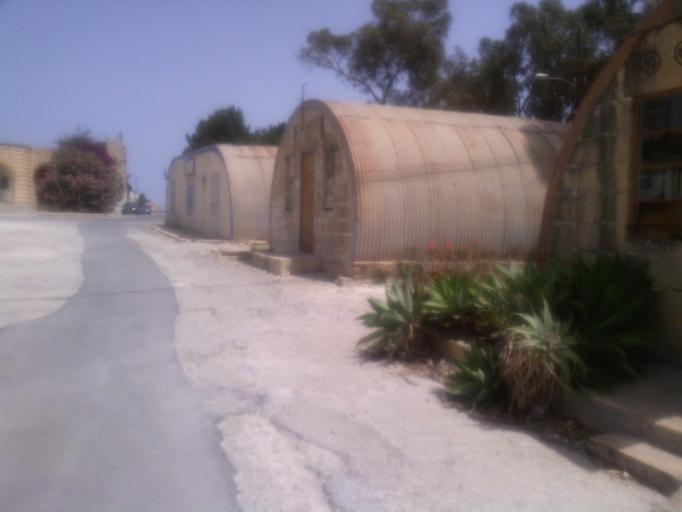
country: MT
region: L-Imdina
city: Imdina
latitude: 35.8909
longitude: 14.4180
